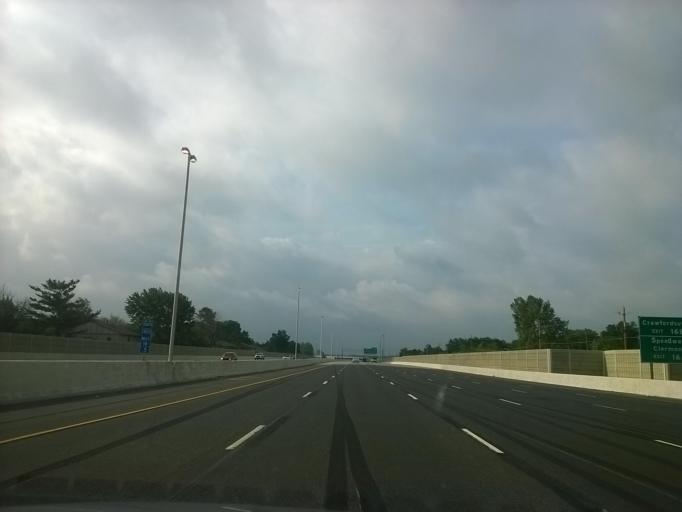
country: US
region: Indiana
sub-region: Marion County
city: Speedway
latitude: 39.8159
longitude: -86.2757
